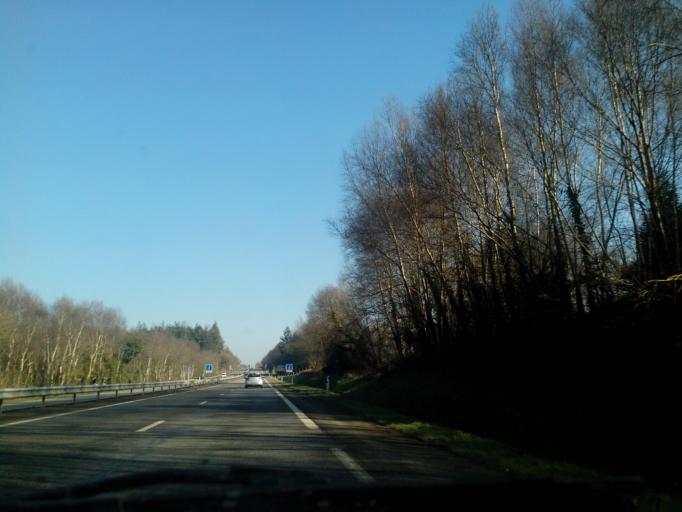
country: FR
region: Brittany
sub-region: Departement du Morbihan
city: Meneac
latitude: 48.1978
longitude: -2.4956
